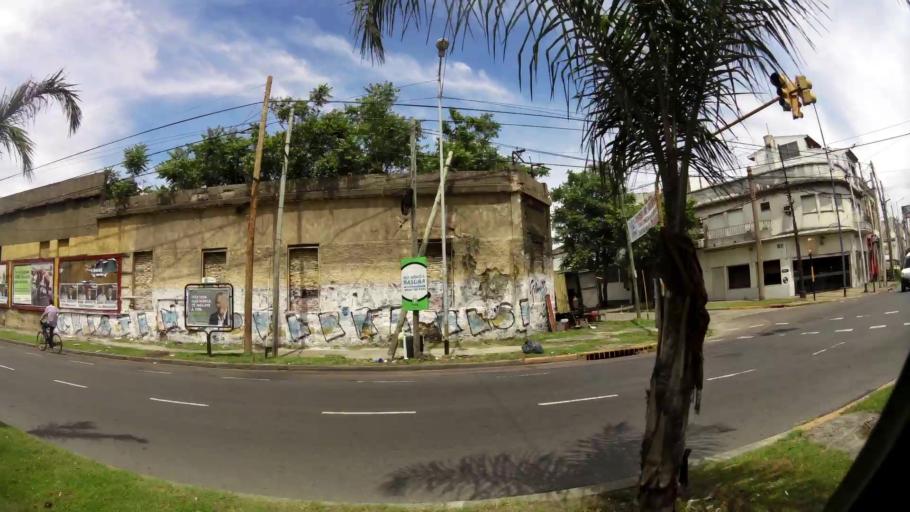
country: AR
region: Buenos Aires
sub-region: Partido de Avellaneda
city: Avellaneda
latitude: -34.6680
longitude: -58.3874
